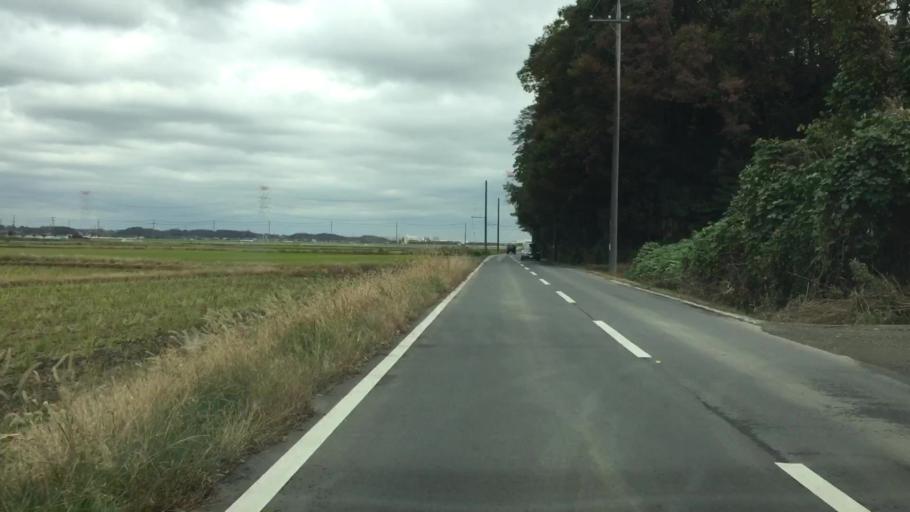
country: JP
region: Chiba
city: Shiroi
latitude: 35.8435
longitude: 140.0921
